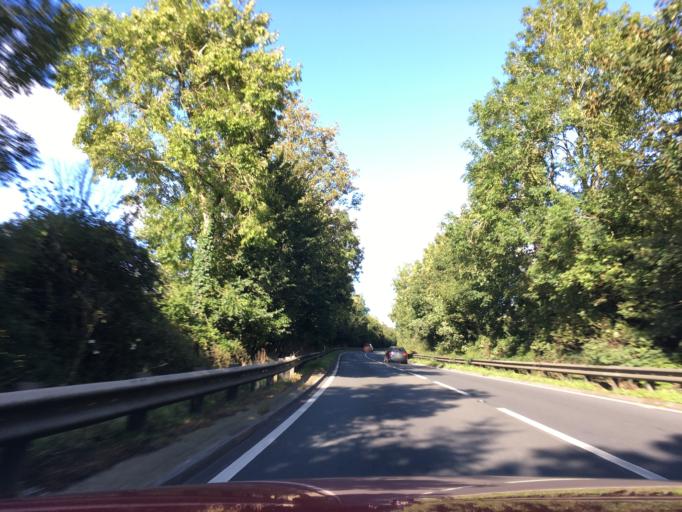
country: GB
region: England
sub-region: Devon
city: Chudleigh
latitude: 50.6285
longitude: -3.5785
